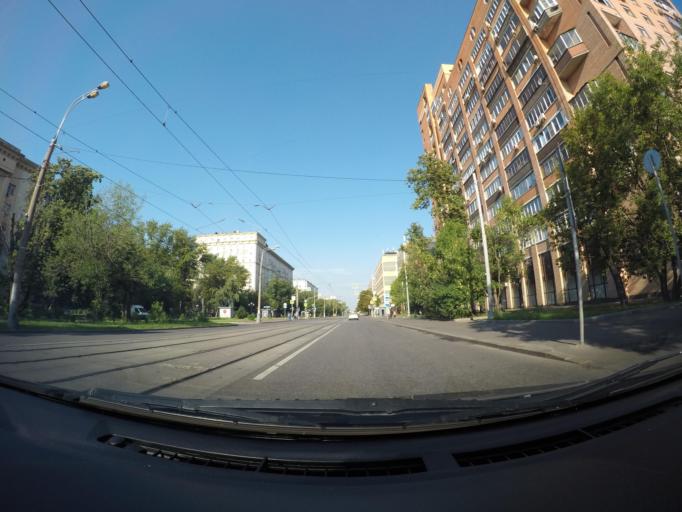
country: RU
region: Moskovskaya
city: Bogorodskoye
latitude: 55.7831
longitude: 37.7401
